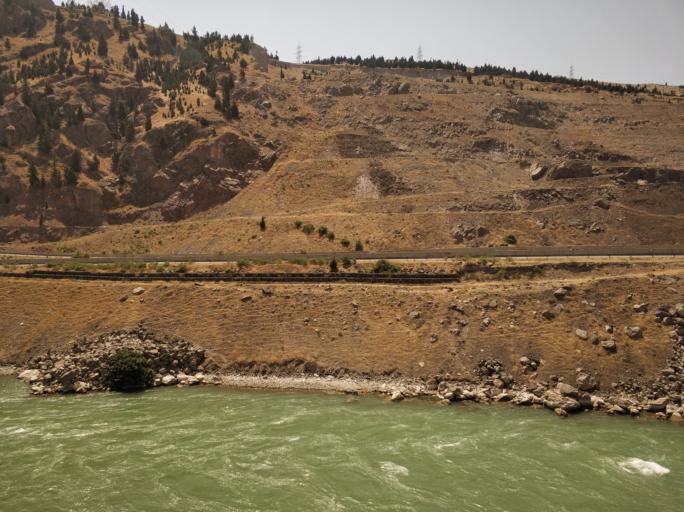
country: IR
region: Gilan
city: Pa'in-e Bazar-e Rudbar
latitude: 36.8356
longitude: 49.4477
